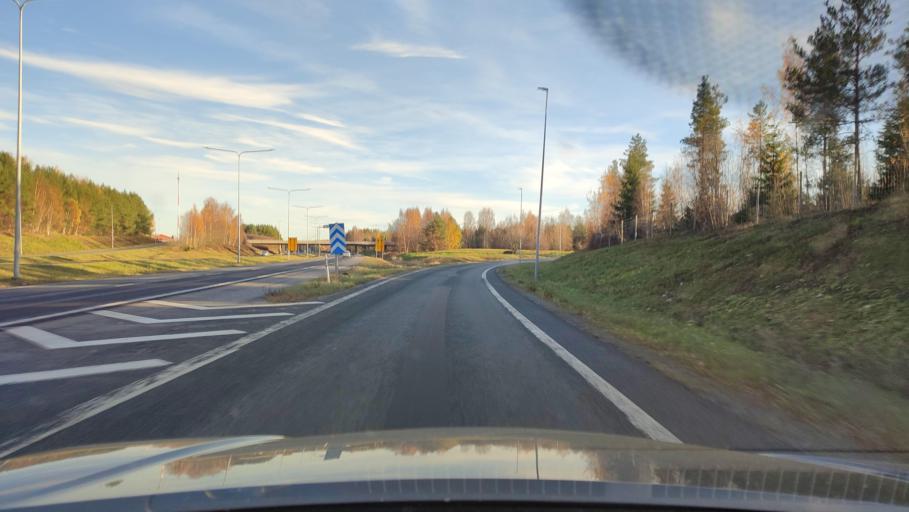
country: FI
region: Ostrobothnia
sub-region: Vaasa
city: Ristinummi
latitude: 63.0303
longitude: 21.7510
